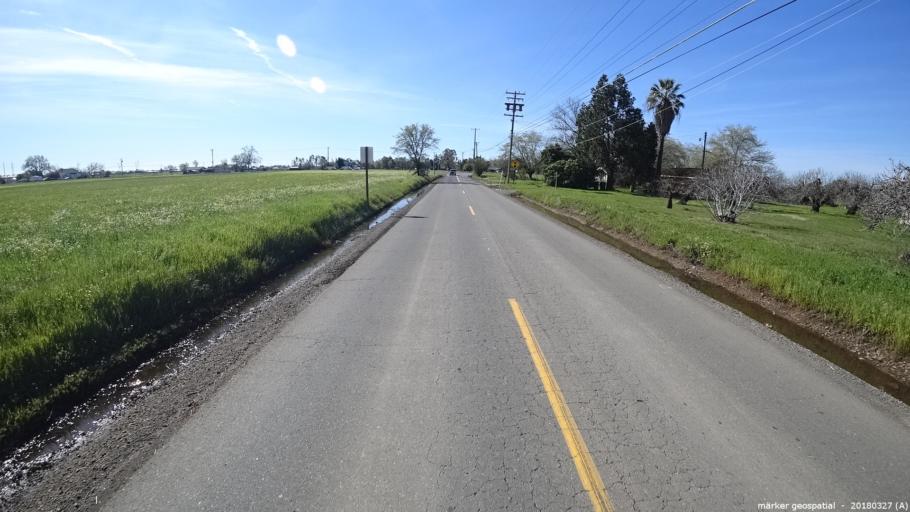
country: US
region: California
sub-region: Sacramento County
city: Vineyard
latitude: 38.4980
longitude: -121.3627
